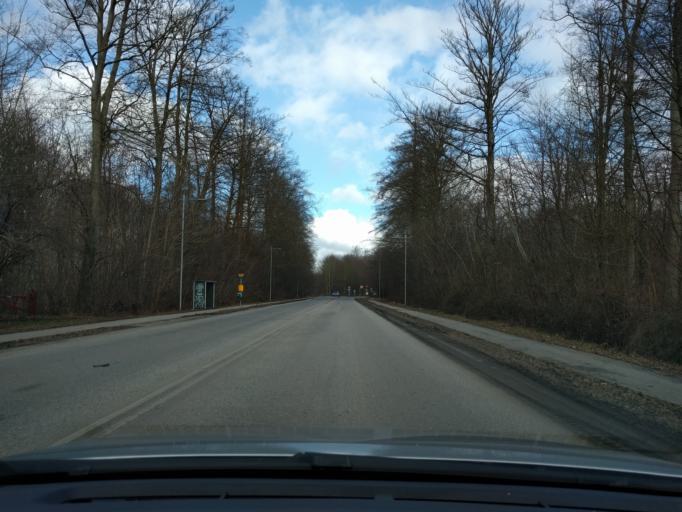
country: DK
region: Zealand
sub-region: Guldborgsund Kommune
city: Nykobing Falster
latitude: 54.7882
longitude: 11.8701
